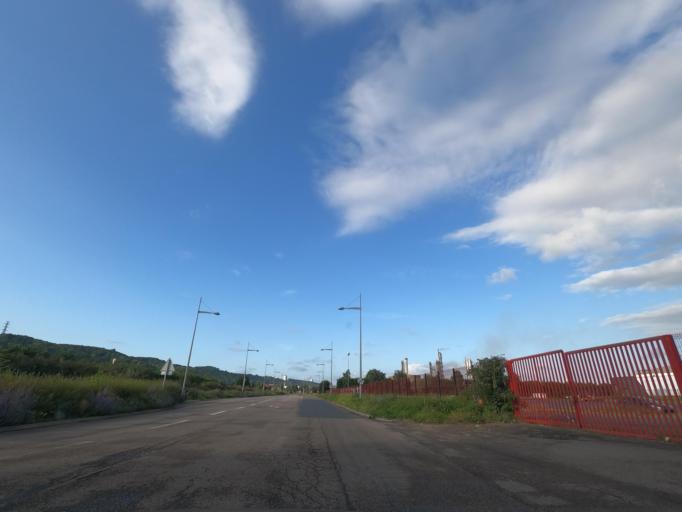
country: FR
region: Haute-Normandie
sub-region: Departement de la Seine-Maritime
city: Canteleu
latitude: 49.4123
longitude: 1.0186
